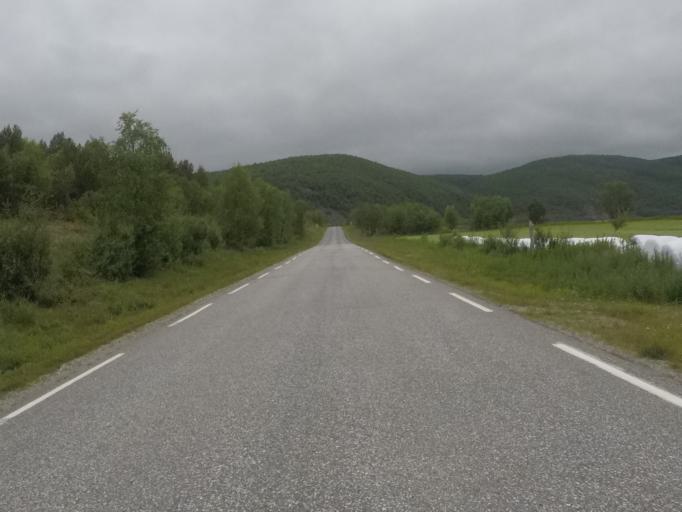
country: NO
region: Finnmark Fylke
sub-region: Karasjok
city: Karasjohka
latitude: 69.6555
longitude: 25.9076
